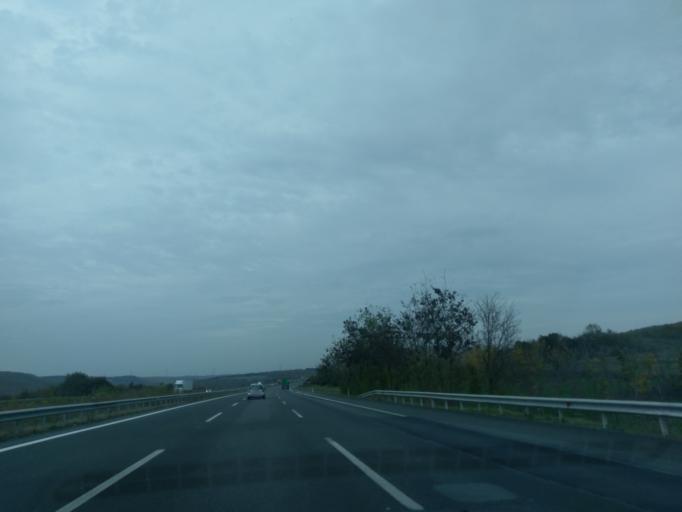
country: TR
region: Istanbul
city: Canta
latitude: 41.1702
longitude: 28.1215
